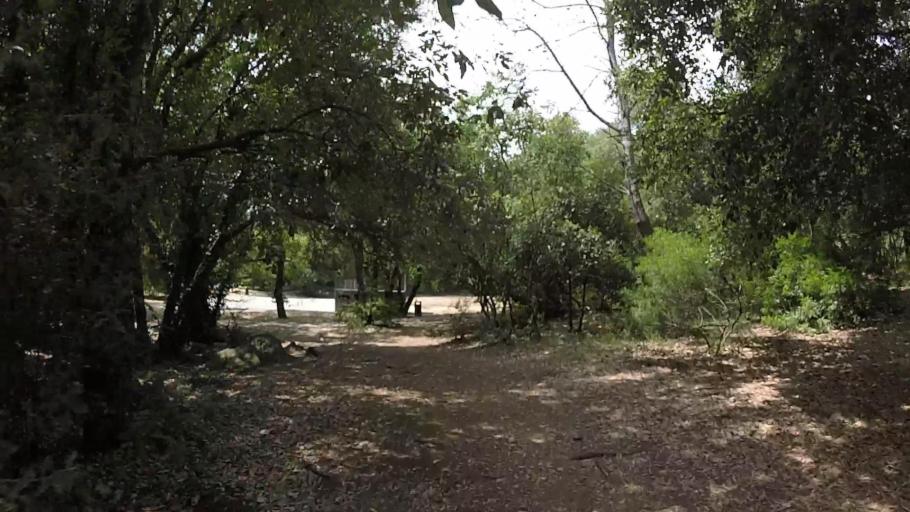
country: FR
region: Provence-Alpes-Cote d'Azur
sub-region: Departement des Alpes-Maritimes
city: Vallauris
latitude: 43.6188
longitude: 7.0472
